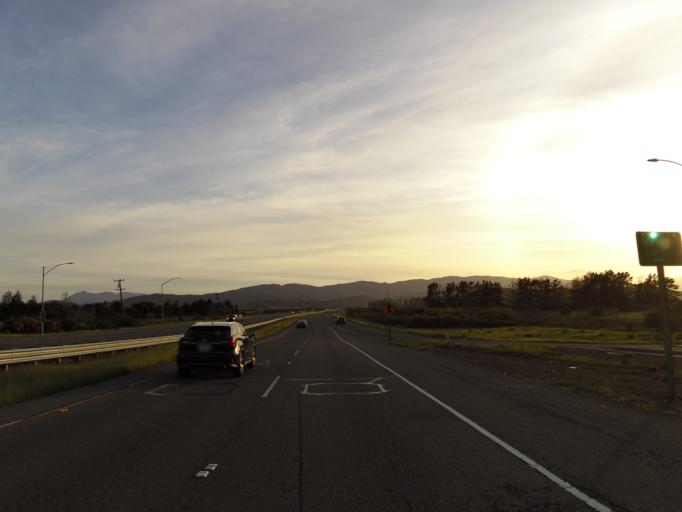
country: US
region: California
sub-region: Marin County
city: Black Point-Green Point
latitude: 38.1045
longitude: -122.5130
